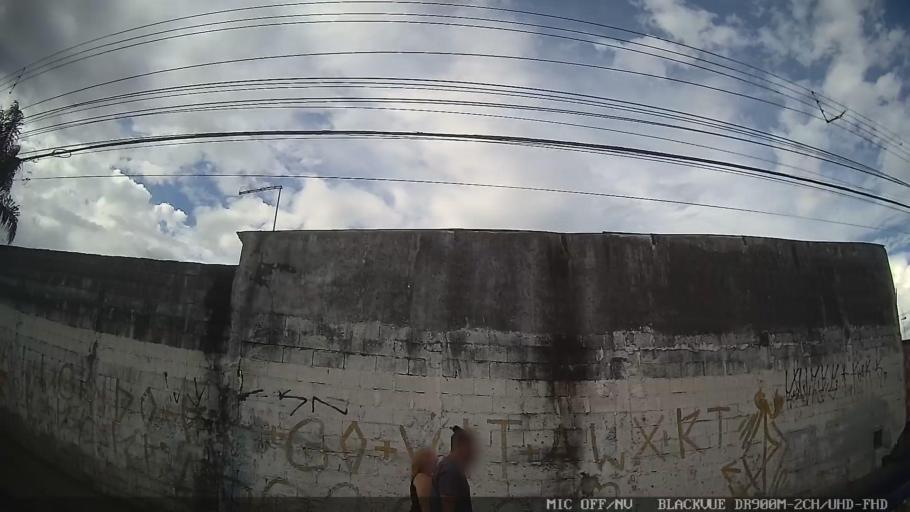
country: BR
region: Sao Paulo
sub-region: Suzano
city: Suzano
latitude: -23.5465
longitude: -46.2481
